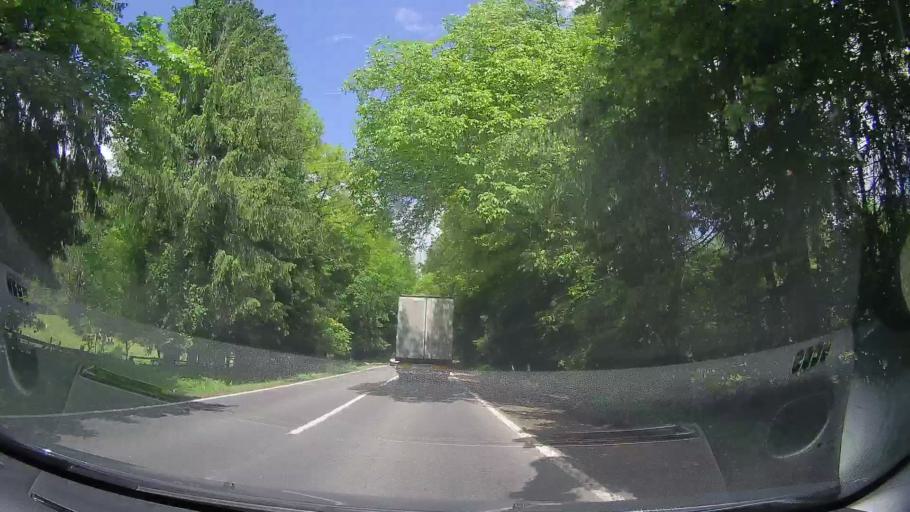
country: RO
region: Prahova
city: Maneciu
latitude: 45.3514
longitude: 25.9475
